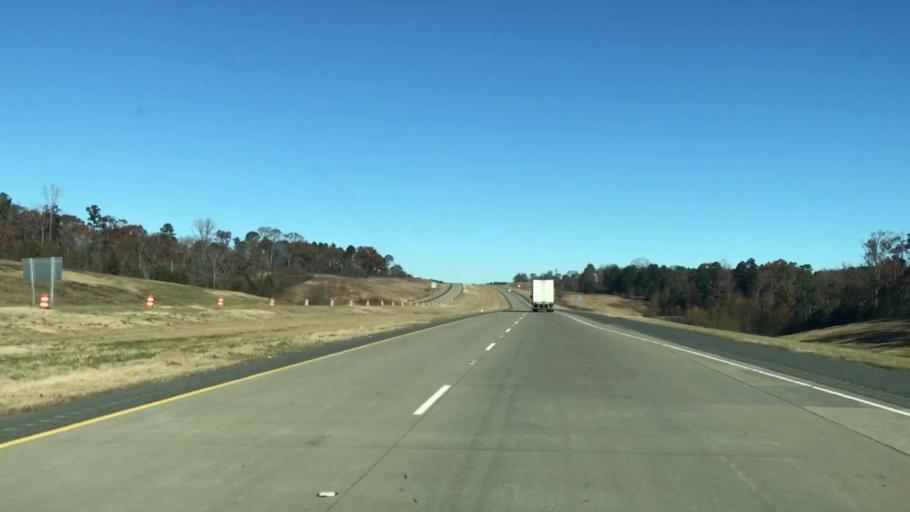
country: US
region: Louisiana
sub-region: Caddo Parish
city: Vivian
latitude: 32.9495
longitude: -93.8989
